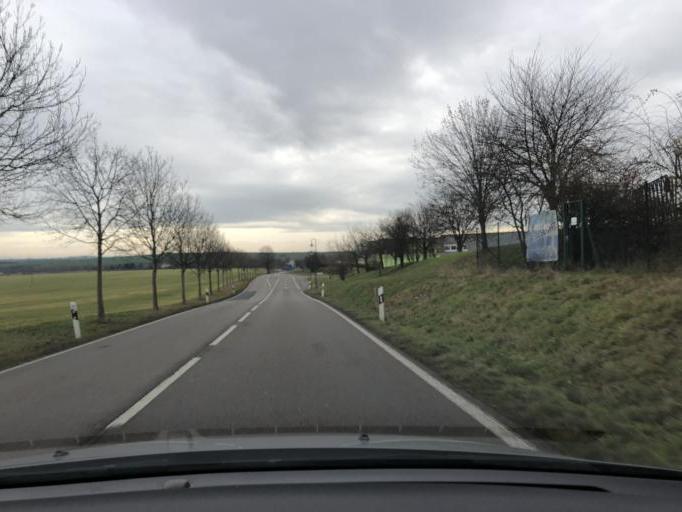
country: DE
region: Saxony
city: Nossen
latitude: 51.0638
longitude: 13.3405
